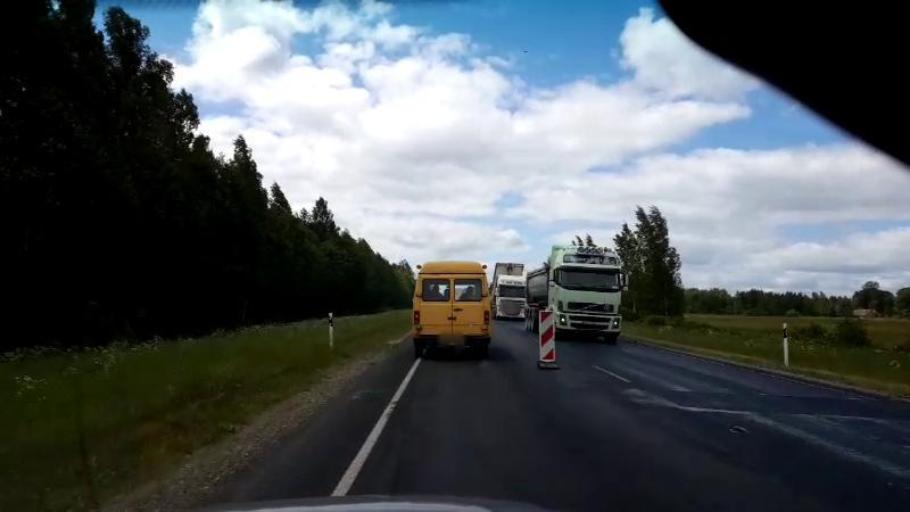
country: LV
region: Salacgrivas
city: Ainazi
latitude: 57.9971
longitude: 24.4763
